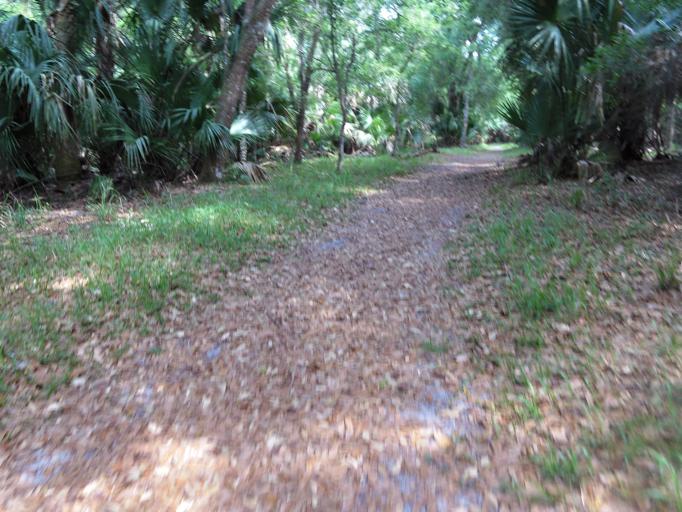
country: US
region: Florida
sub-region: Flagler County
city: Flagler Beach
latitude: 29.3952
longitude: -81.1341
